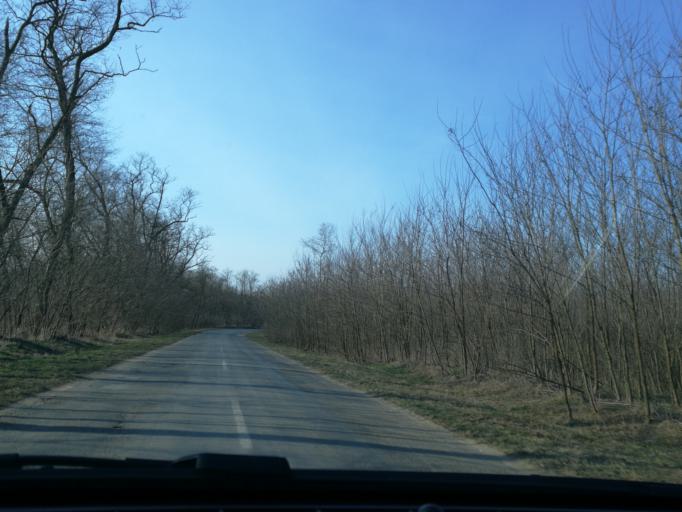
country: HU
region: Szabolcs-Szatmar-Bereg
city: Levelek
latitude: 48.0311
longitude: 21.9703
